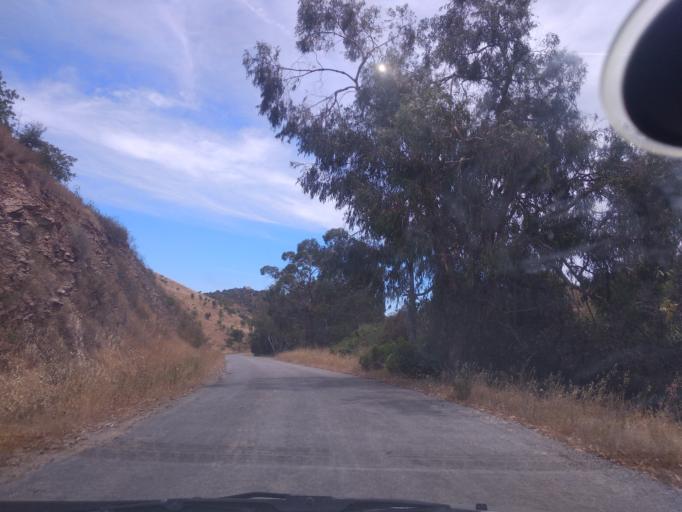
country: PT
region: Faro
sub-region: Olhao
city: Moncarapacho
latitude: 37.1665
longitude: -7.8021
